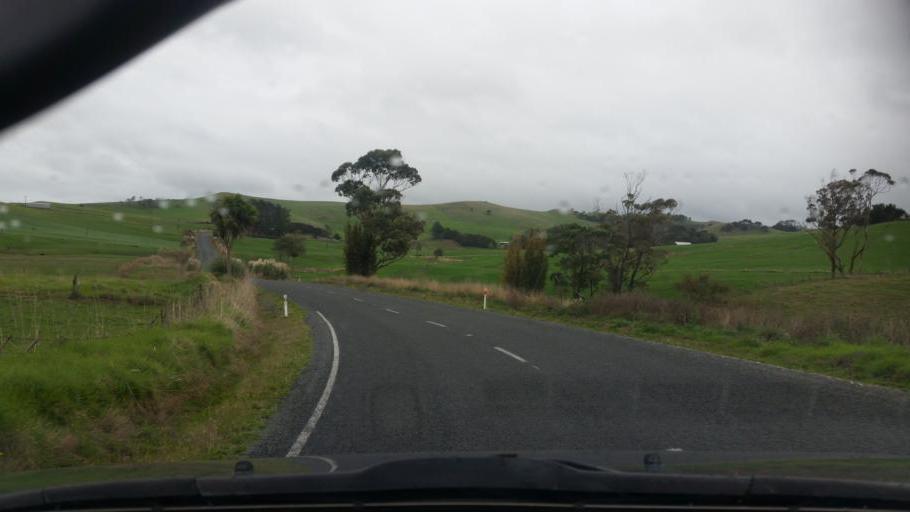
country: NZ
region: Northland
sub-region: Kaipara District
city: Dargaville
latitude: -36.0092
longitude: 173.9743
